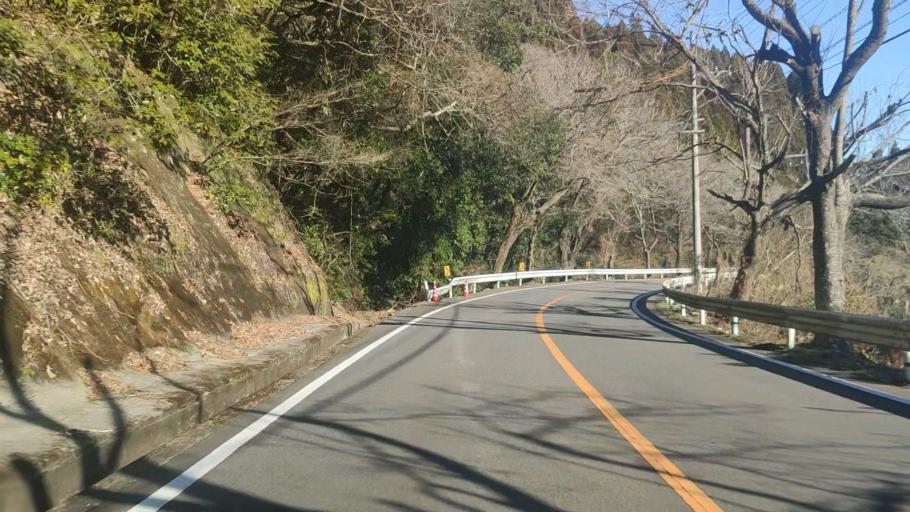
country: JP
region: Miyazaki
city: Nobeoka
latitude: 32.6387
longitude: 131.7429
